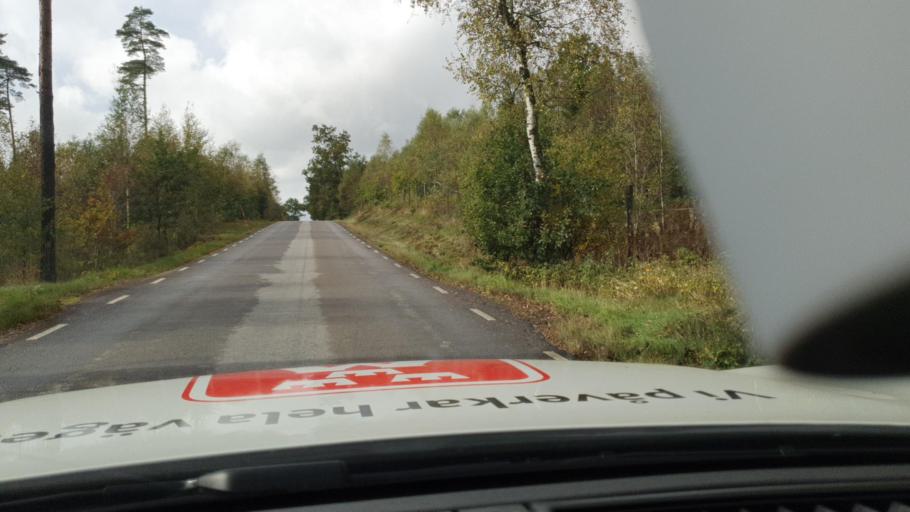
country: SE
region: Halland
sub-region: Hylte Kommun
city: Torup
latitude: 57.0206
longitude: 13.0550
